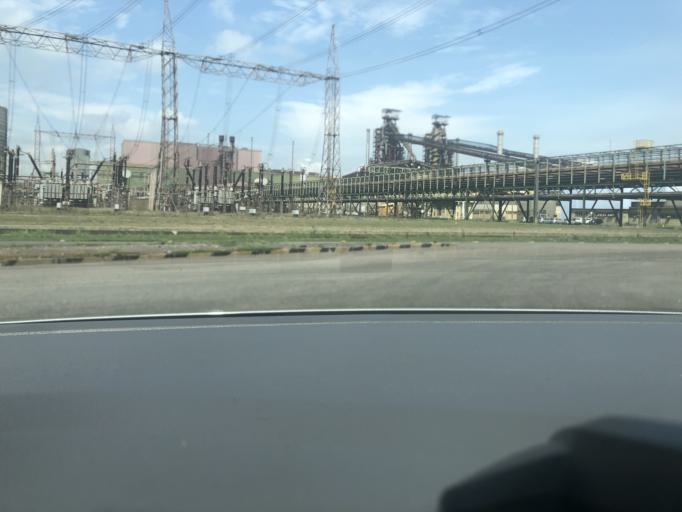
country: BR
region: Rio de Janeiro
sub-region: Itaguai
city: Itaguai
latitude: -22.9090
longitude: -43.7446
